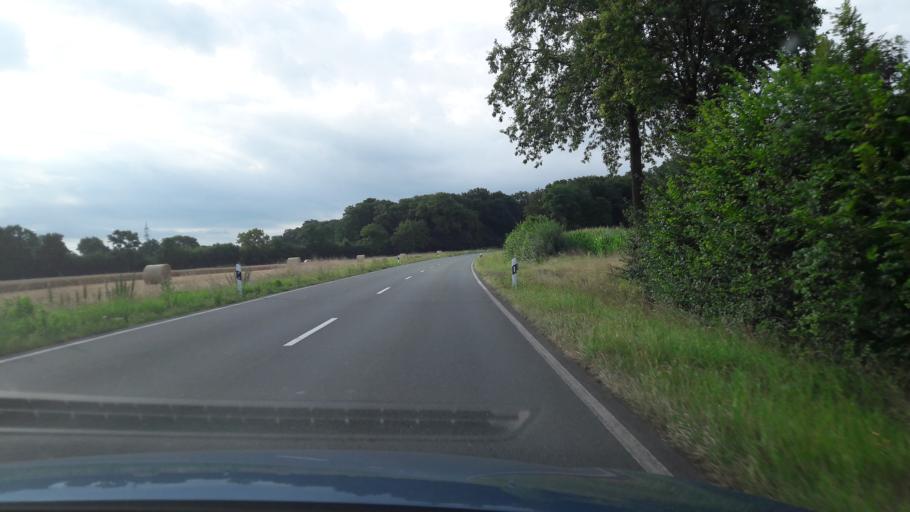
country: DE
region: North Rhine-Westphalia
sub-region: Regierungsbezirk Munster
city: Ennigerloh
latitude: 51.8557
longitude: 7.9841
